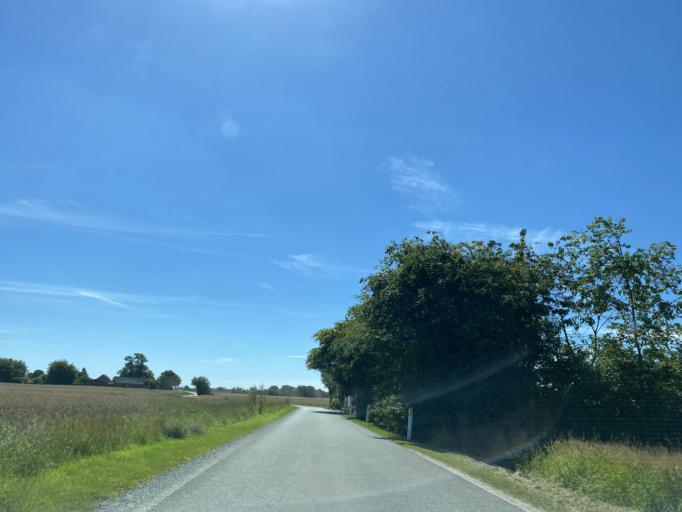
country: DK
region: South Denmark
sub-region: Fredericia Kommune
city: Taulov
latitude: 55.6071
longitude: 9.5382
